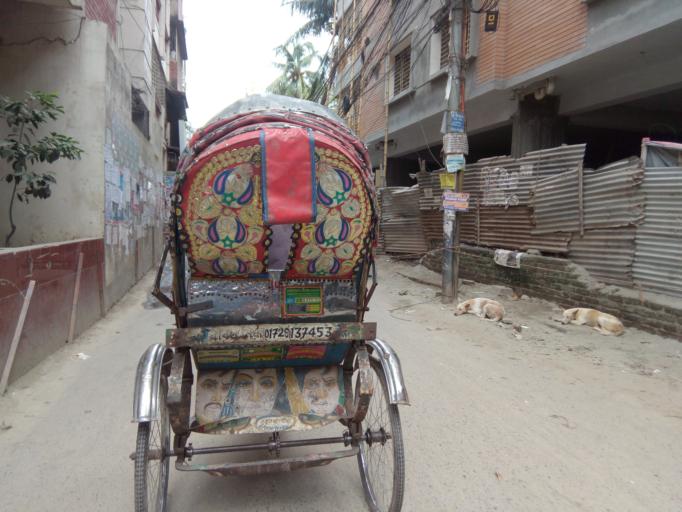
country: BD
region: Dhaka
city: Azimpur
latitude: 23.7478
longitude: 90.3907
